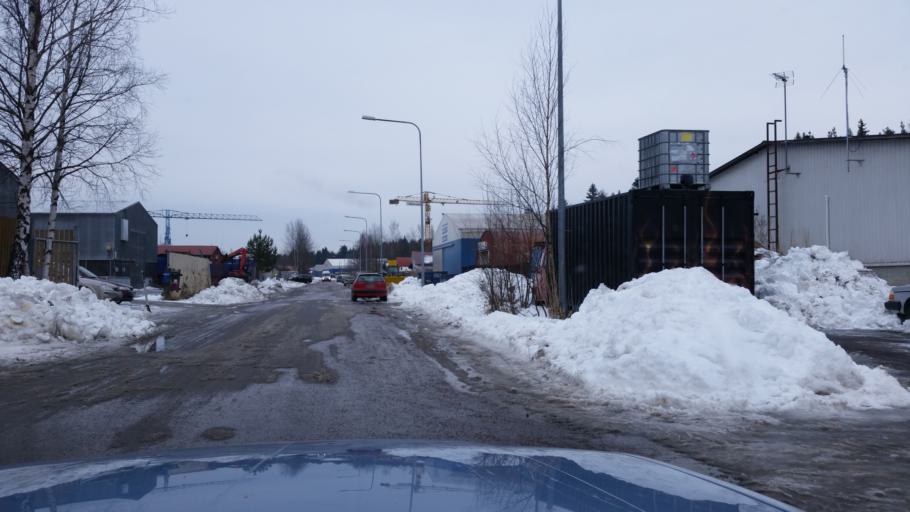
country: FI
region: Uusimaa
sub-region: Helsinki
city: Vantaa
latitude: 60.2530
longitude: 25.0609
